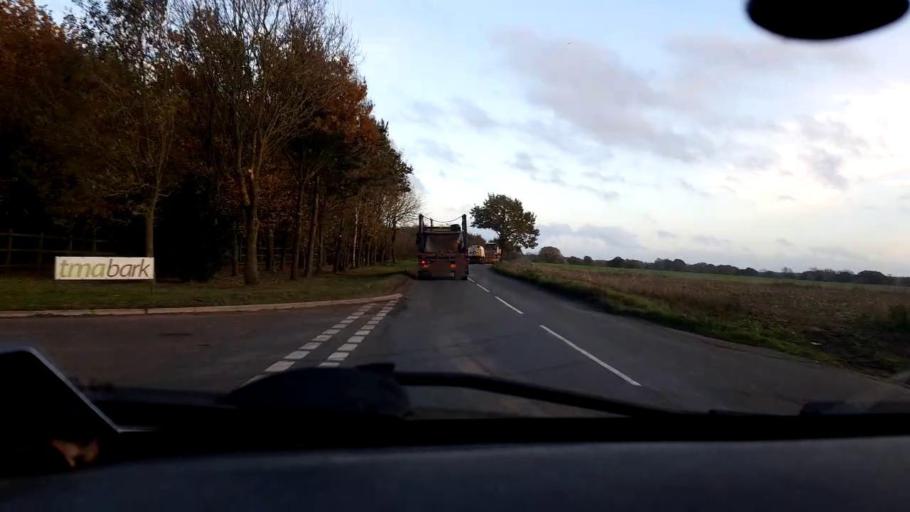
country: GB
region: England
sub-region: Norfolk
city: Mattishall
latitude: 52.6939
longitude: 1.0940
